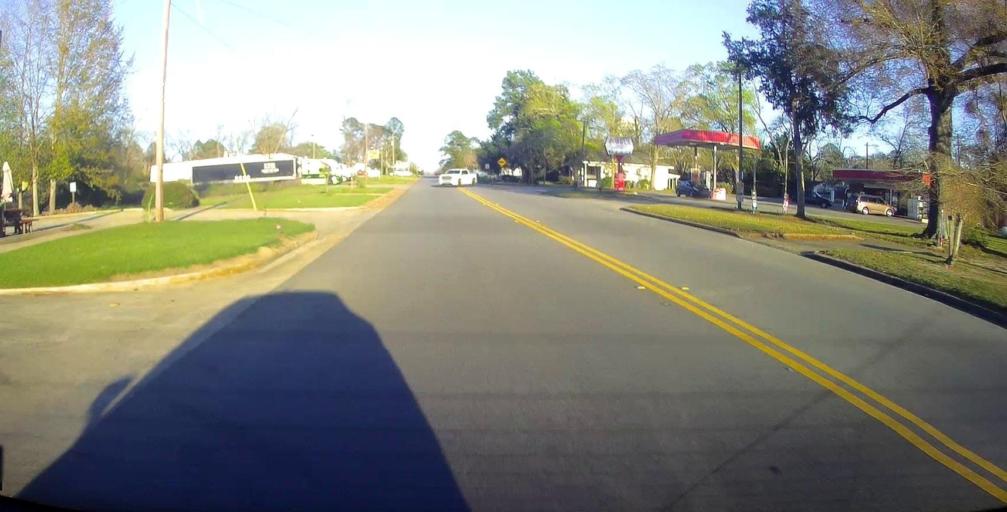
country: US
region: Georgia
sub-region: Wilcox County
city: Rochelle
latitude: 31.9509
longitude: -83.4522
